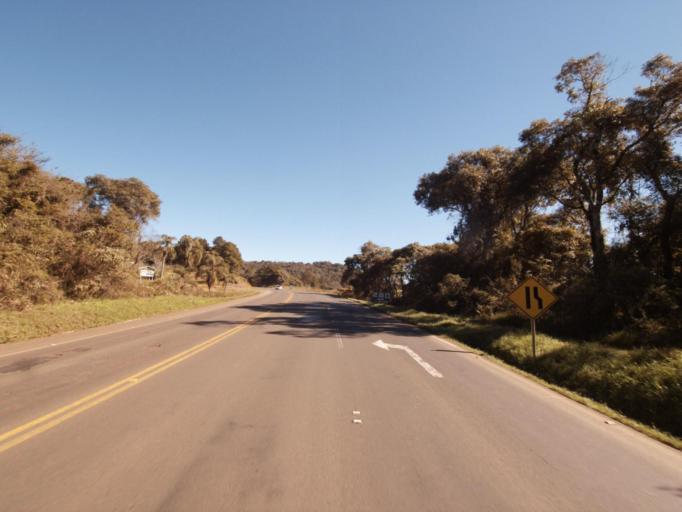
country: BR
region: Santa Catarina
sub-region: Joacaba
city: Joacaba
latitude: -27.1567
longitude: -51.5928
